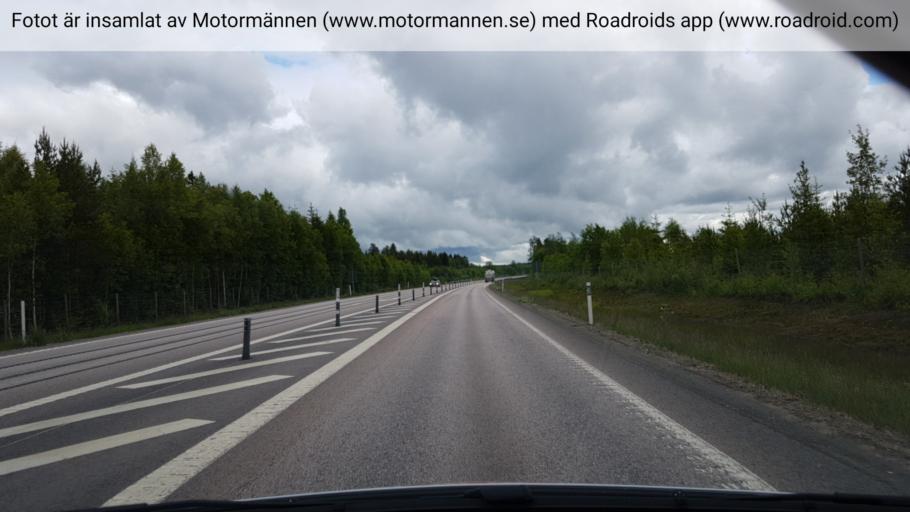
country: SE
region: Vaesterbotten
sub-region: Nordmalings Kommun
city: Nordmaling
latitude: 63.5638
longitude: 19.4297
